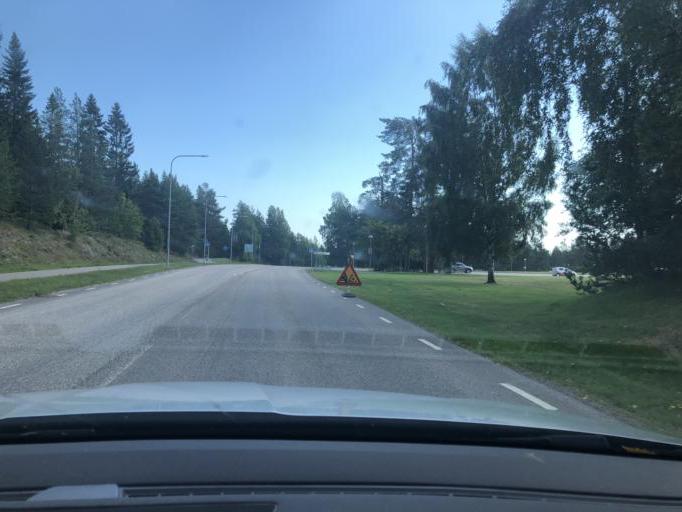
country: SE
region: Vaesternorrland
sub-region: Sundsvalls Kommun
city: Sundsvall
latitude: 62.4107
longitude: 17.3073
